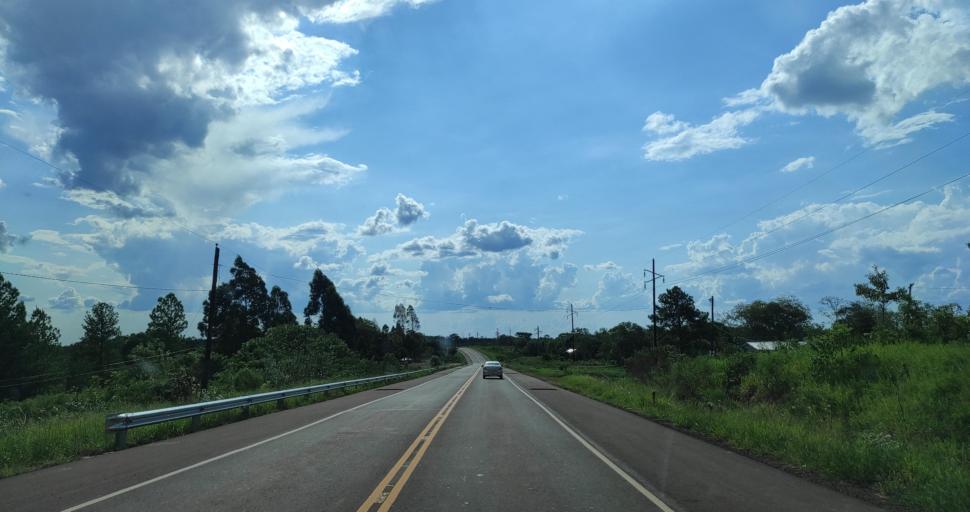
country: AR
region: Misiones
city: Bernardo de Irigoyen
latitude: -26.2992
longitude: -53.8041
